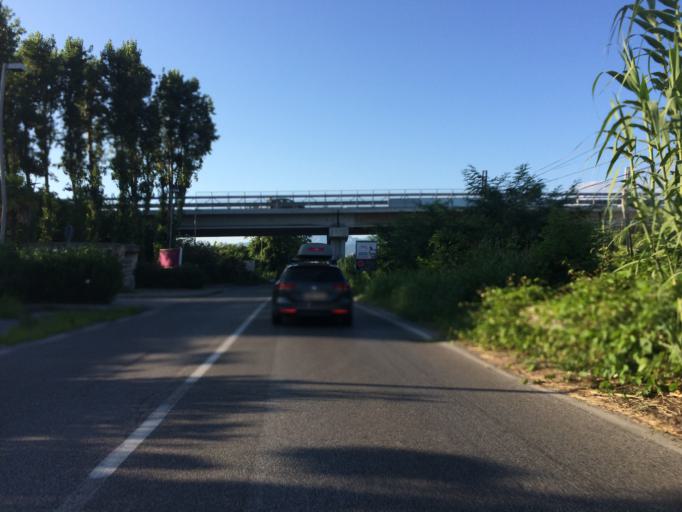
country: IT
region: Tuscany
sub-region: Provincia di Lucca
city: Viareggio
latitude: 43.8880
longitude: 10.2503
